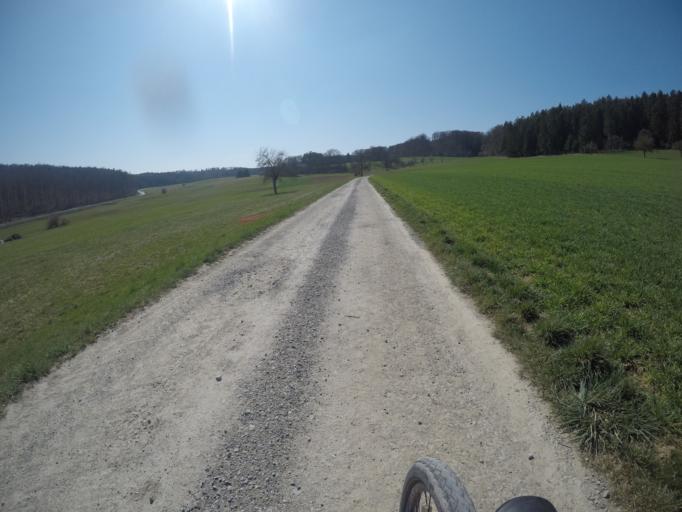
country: DE
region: Baden-Wuerttemberg
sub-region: Karlsruhe Region
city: Gechingen
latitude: 48.6897
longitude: 8.8081
